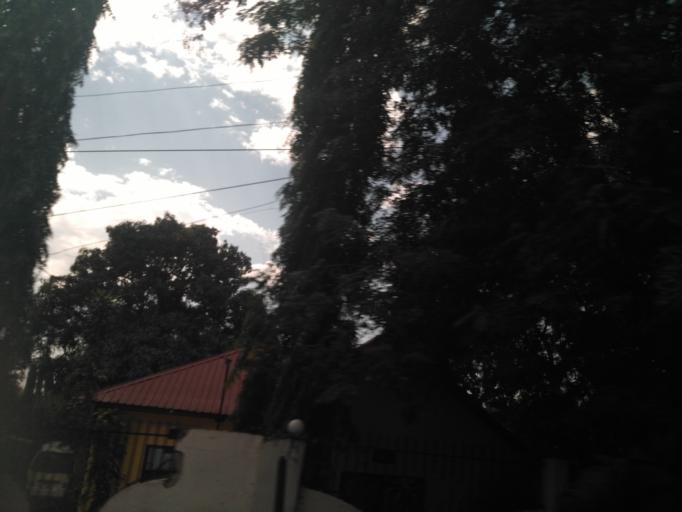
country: TZ
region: Mwanza
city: Mwanza
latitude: -2.5132
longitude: 32.9086
